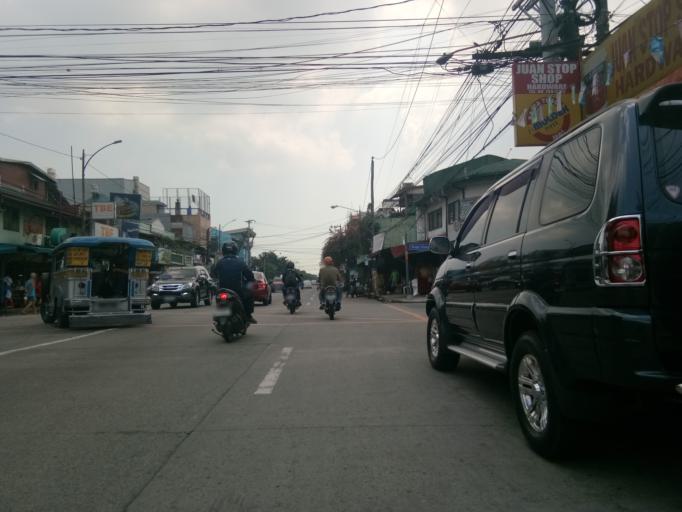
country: PH
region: Metro Manila
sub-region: Marikina
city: Calumpang
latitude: 14.6189
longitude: 121.0640
